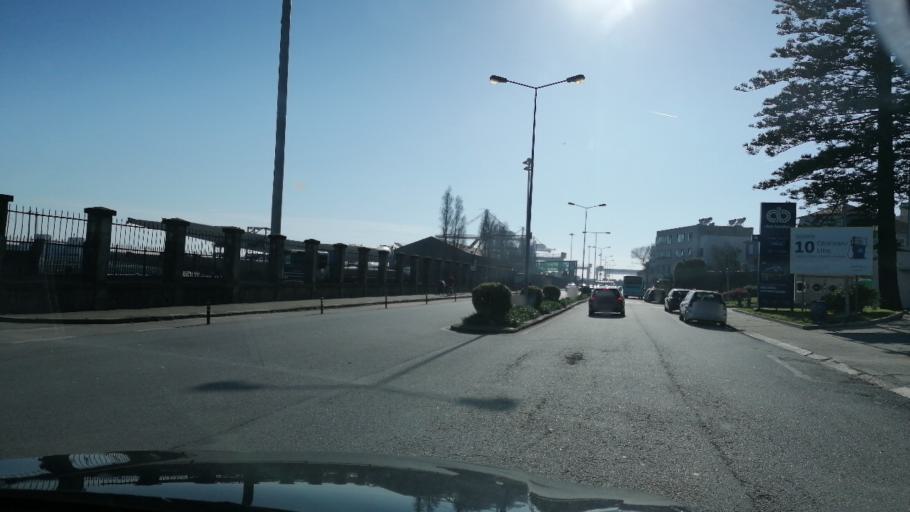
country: PT
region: Porto
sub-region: Matosinhos
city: Leca da Palmeira
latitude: 41.1892
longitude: -8.6969
